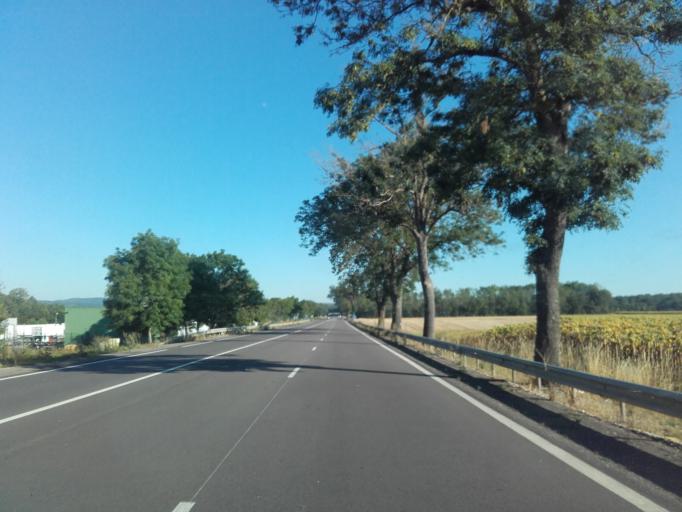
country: FR
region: Bourgogne
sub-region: Departement de Saone-et-Loire
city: Fontaines
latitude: 46.8614
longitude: 4.7977
